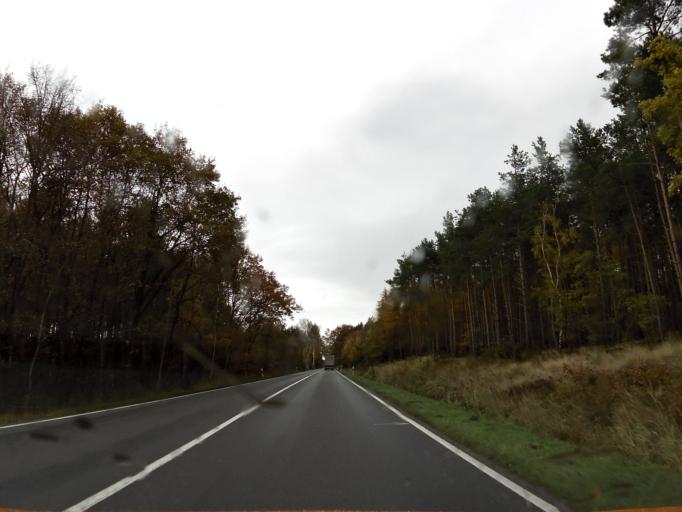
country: DE
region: Saxony-Anhalt
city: Kalbe
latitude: 52.6295
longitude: 11.3085
